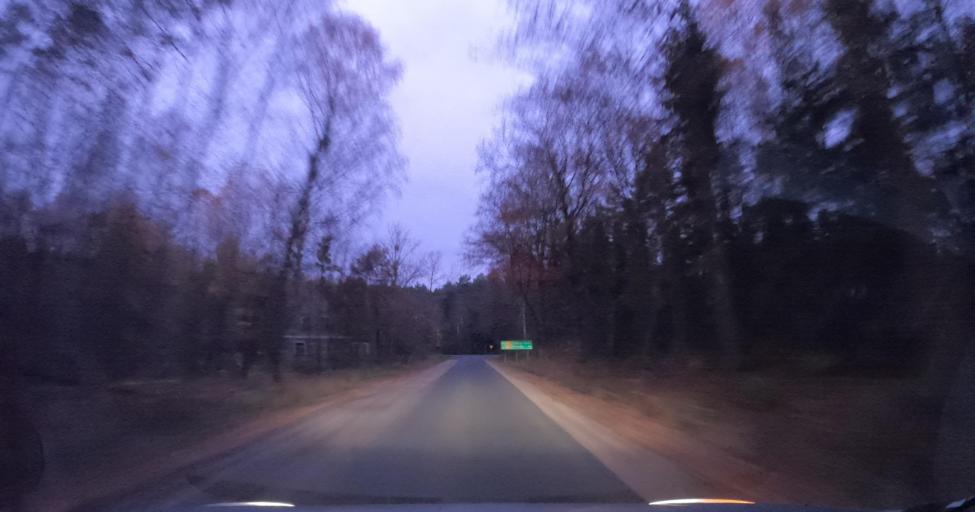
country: PL
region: West Pomeranian Voivodeship
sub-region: Powiat bialogardzki
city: Tychowo
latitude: 53.9007
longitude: 16.2231
